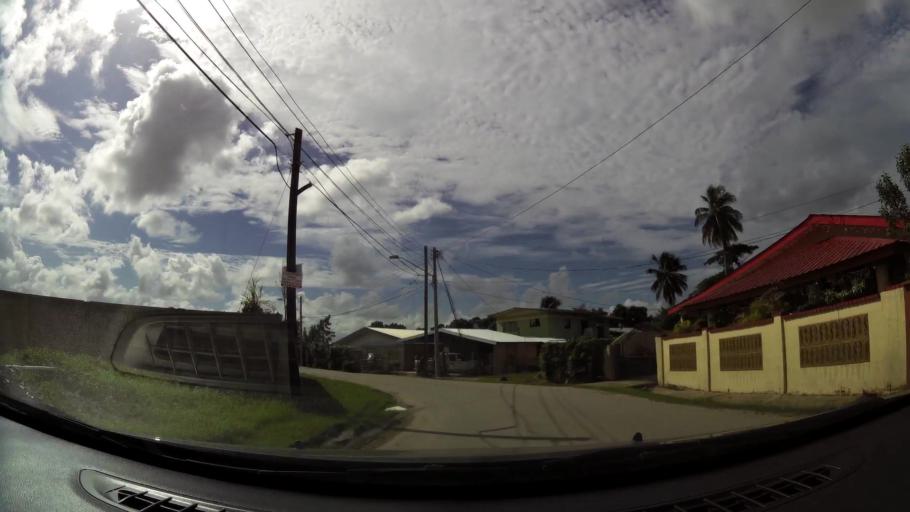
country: TT
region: Chaguanas
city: Chaguanas
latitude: 10.5089
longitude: -61.3866
